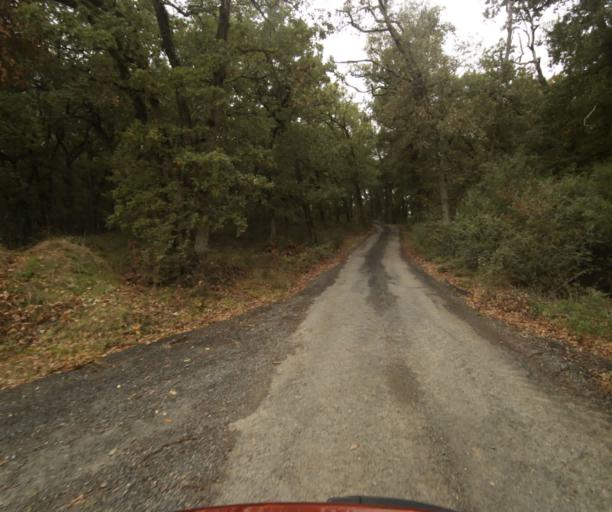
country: FR
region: Midi-Pyrenees
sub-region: Departement de la Haute-Garonne
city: Launac
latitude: 43.7787
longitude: 1.2252
